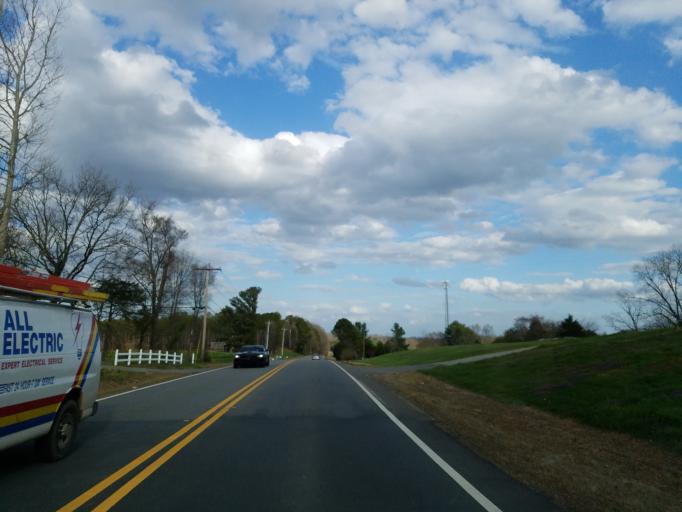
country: US
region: Georgia
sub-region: Bartow County
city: Rydal
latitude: 34.4481
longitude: -84.8066
